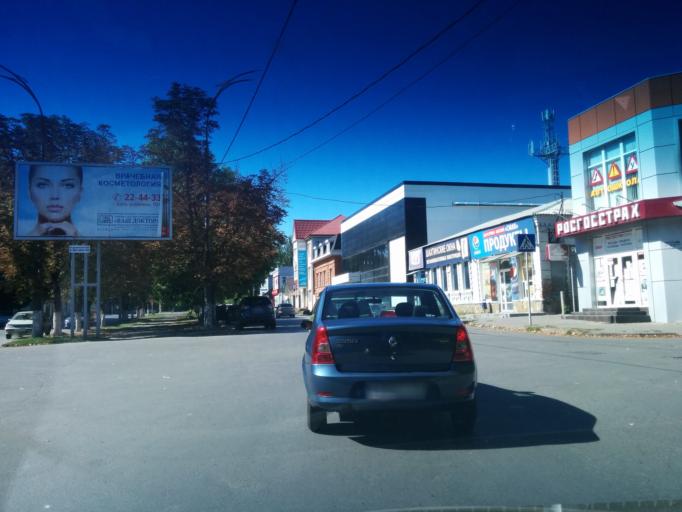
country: RU
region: Rostov
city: Shakhty
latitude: 47.7132
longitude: 40.2121
